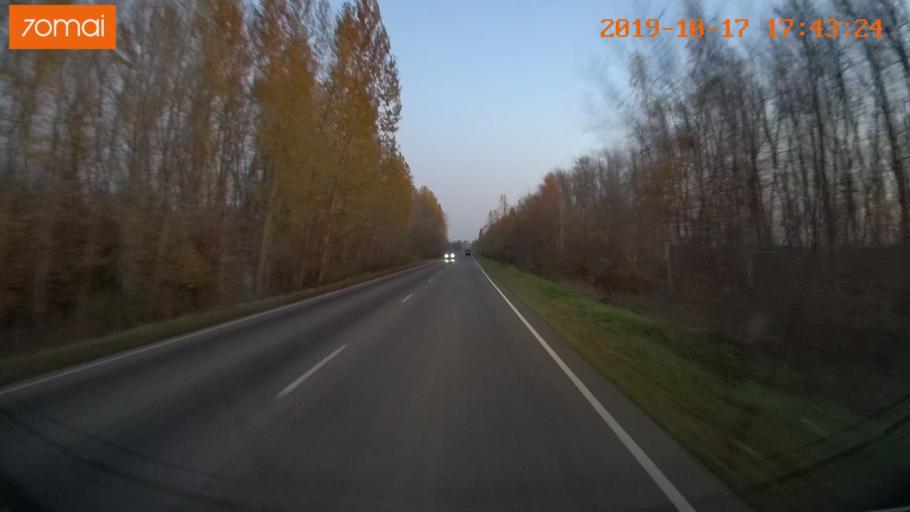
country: RU
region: Tula
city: Yepifan'
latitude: 53.7596
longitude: 38.6610
